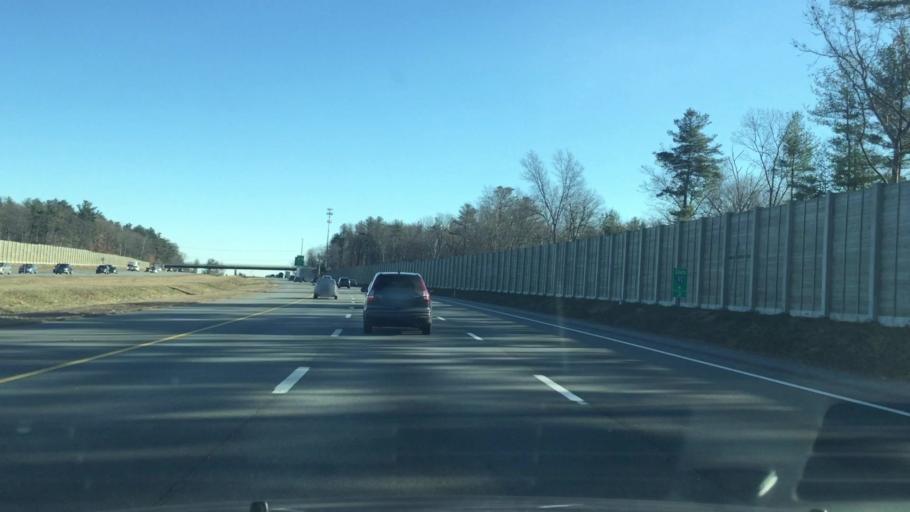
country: US
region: New Hampshire
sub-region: Rockingham County
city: Windham
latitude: 42.7849
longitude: -71.2633
